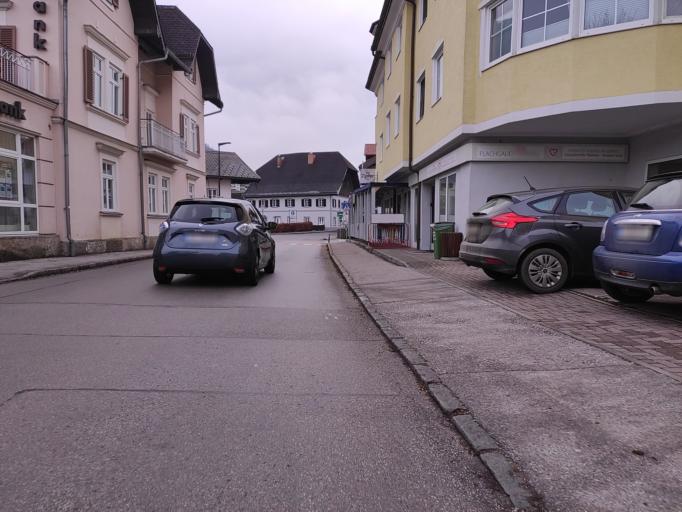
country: AT
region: Salzburg
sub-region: Politischer Bezirk Salzburg-Umgebung
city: Mattsee
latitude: 47.9693
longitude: 13.1039
